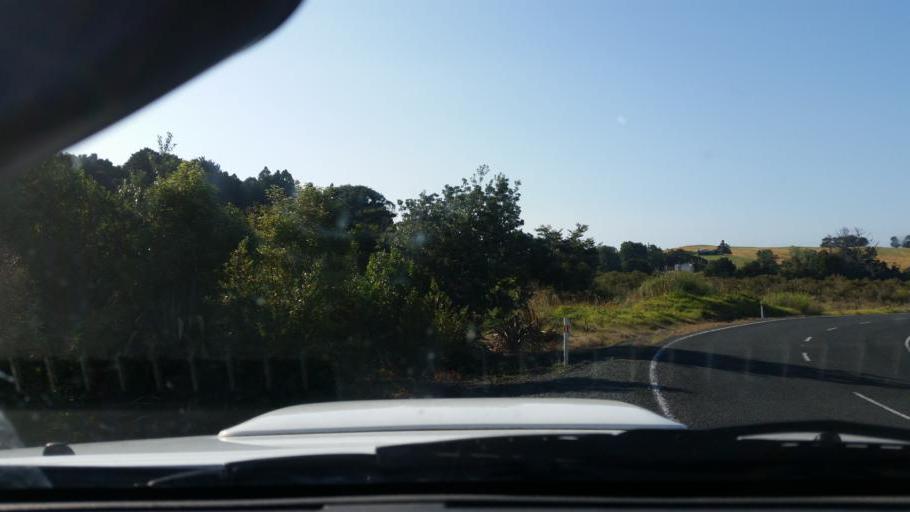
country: NZ
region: Northland
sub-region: Whangarei
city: Ruakaka
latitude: -36.1114
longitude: 174.2302
